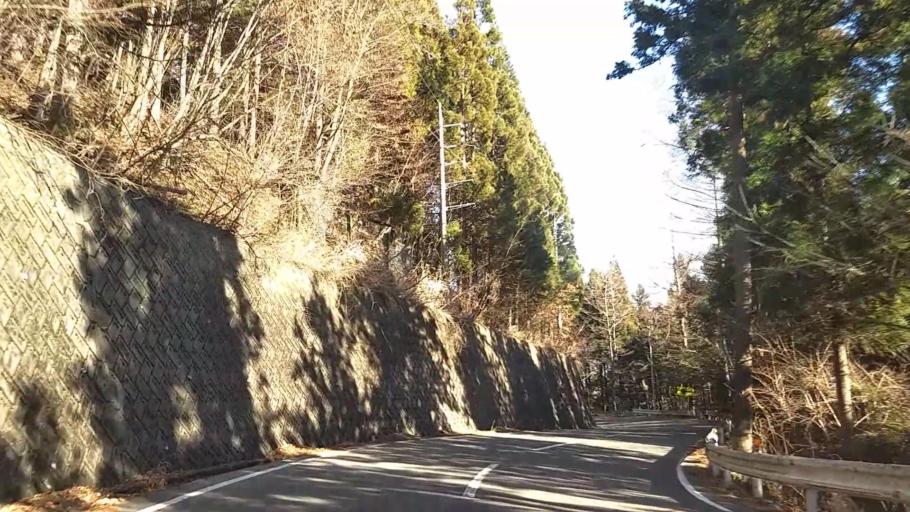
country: JP
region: Yamanashi
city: Otsuki
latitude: 35.5111
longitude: 138.9774
